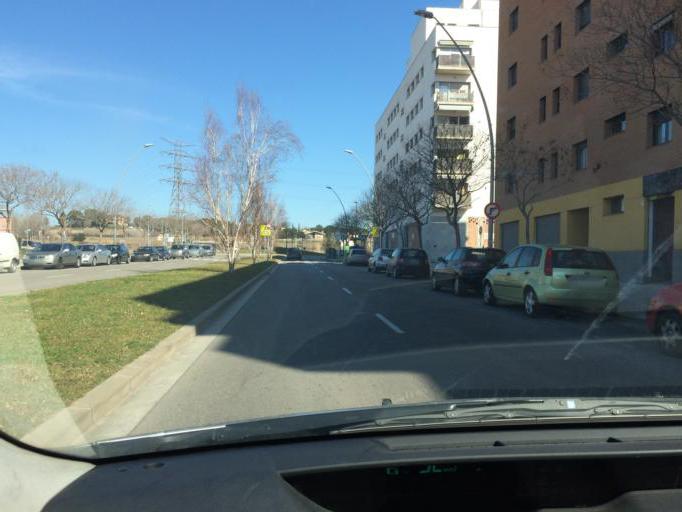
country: ES
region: Catalonia
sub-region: Provincia de Barcelona
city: Manresa
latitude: 41.7408
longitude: 1.8388
